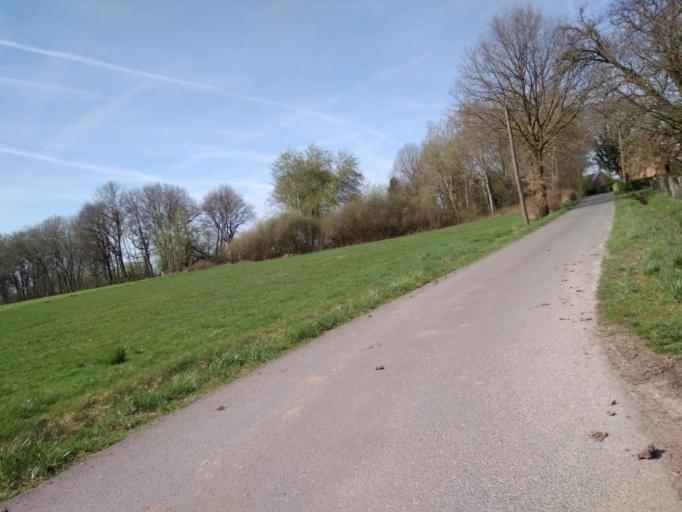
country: DE
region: North Rhine-Westphalia
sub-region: Regierungsbezirk Dusseldorf
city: Schermbeck
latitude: 51.6602
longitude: 6.8608
